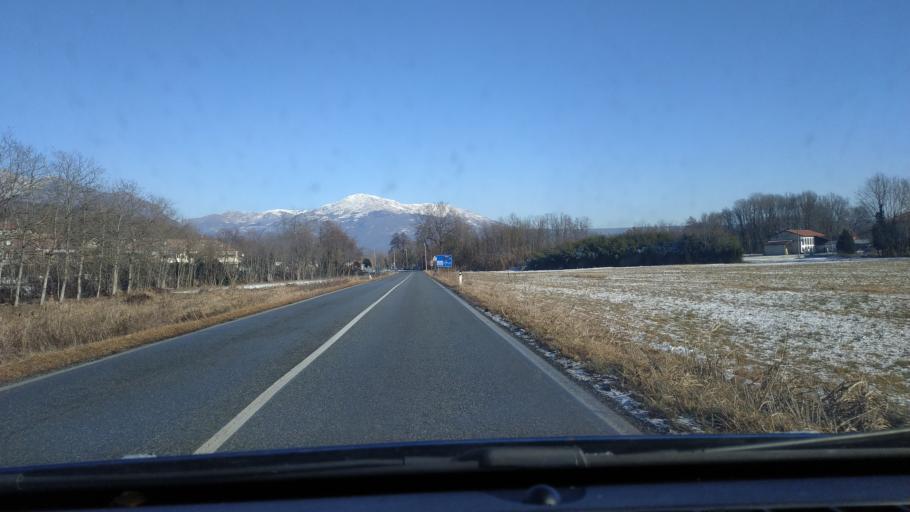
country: IT
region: Piedmont
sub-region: Provincia di Torino
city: Colleretto Giacosa
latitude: 45.4297
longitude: 7.8022
